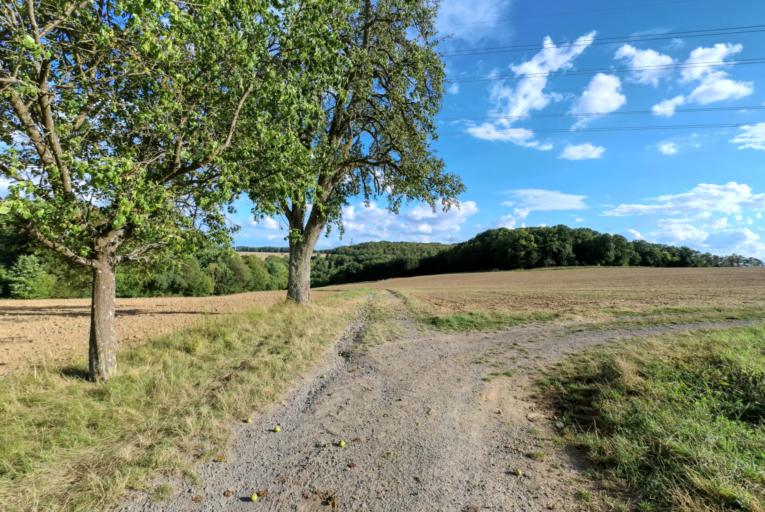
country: DE
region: Baden-Wuerttemberg
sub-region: Karlsruhe Region
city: Mosbach
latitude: 49.3425
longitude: 9.1621
